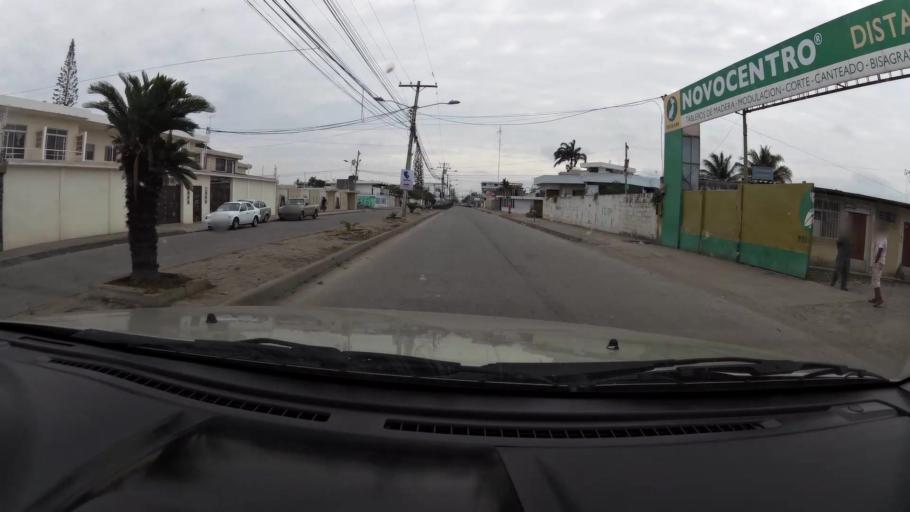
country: EC
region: El Oro
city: Machala
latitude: -3.2489
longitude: -79.9566
